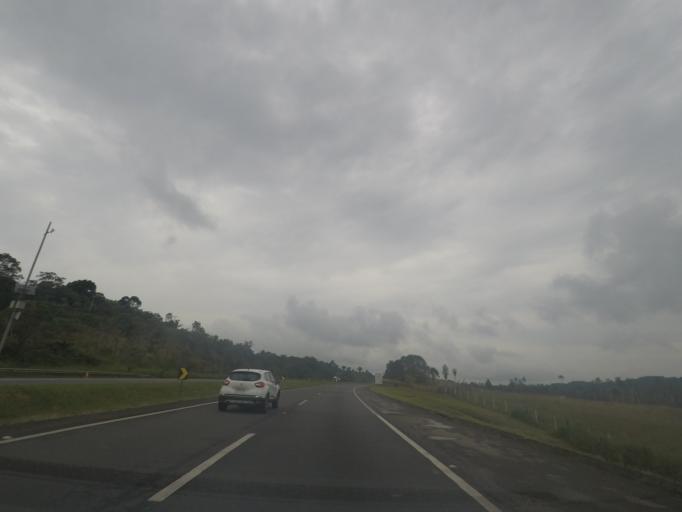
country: BR
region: Sao Paulo
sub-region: Cajati
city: Cajati
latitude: -24.9227
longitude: -48.2615
